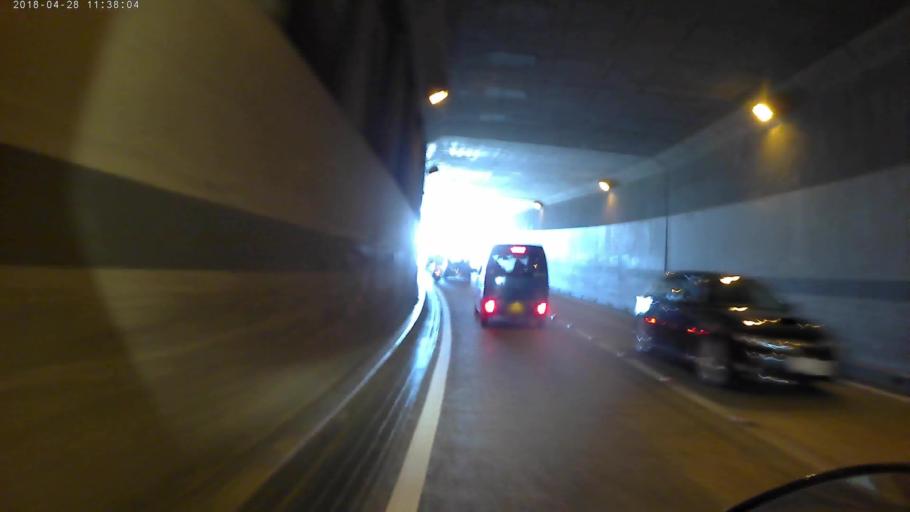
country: JP
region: Kanagawa
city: Fujisawa
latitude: 35.3370
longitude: 139.4493
